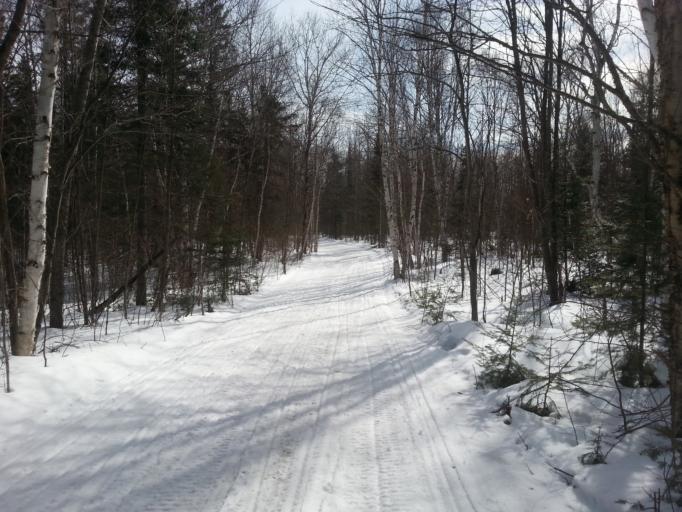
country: CA
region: Ontario
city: Greater Sudbury
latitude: 46.3465
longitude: -80.9011
